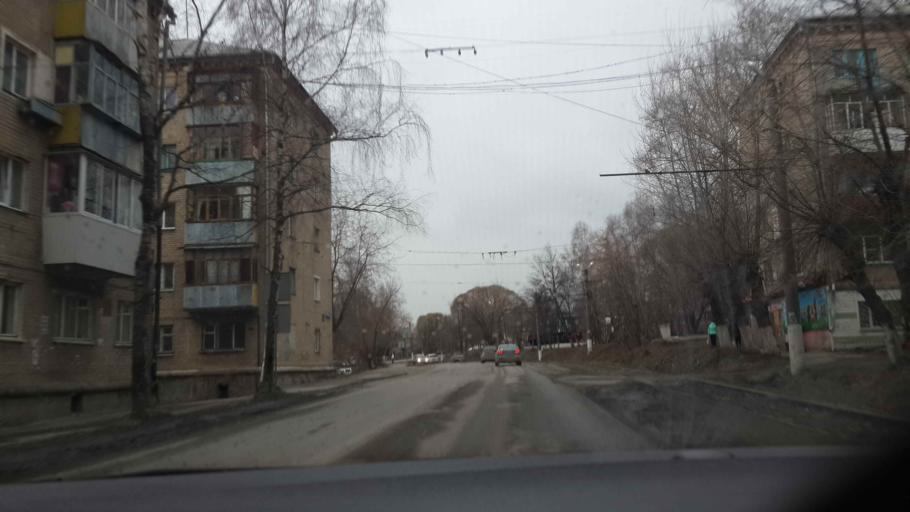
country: RU
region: Chelyabinsk
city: Zlatoust
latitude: 55.1982
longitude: 59.7131
